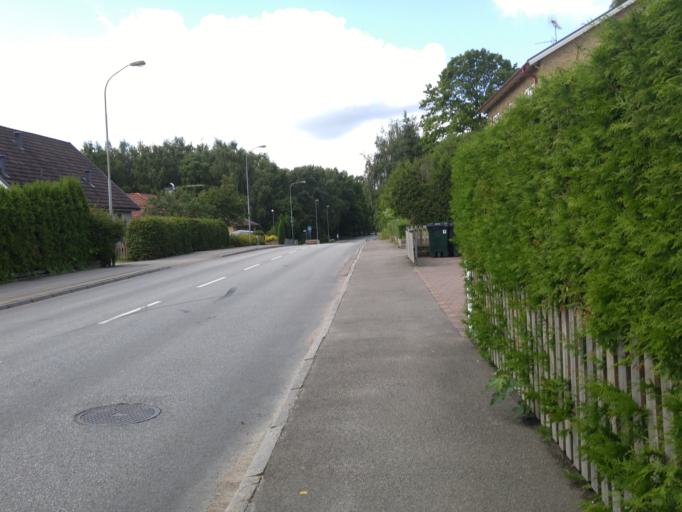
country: SE
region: Skane
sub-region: Hoors Kommun
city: Hoeoer
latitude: 55.9279
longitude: 13.5376
